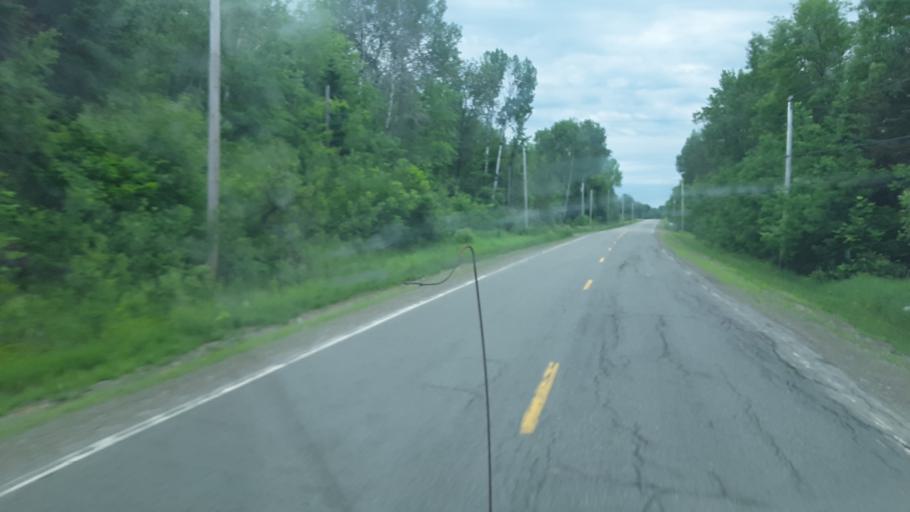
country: US
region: Maine
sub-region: Penobscot County
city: Patten
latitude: 45.8579
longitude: -68.3276
